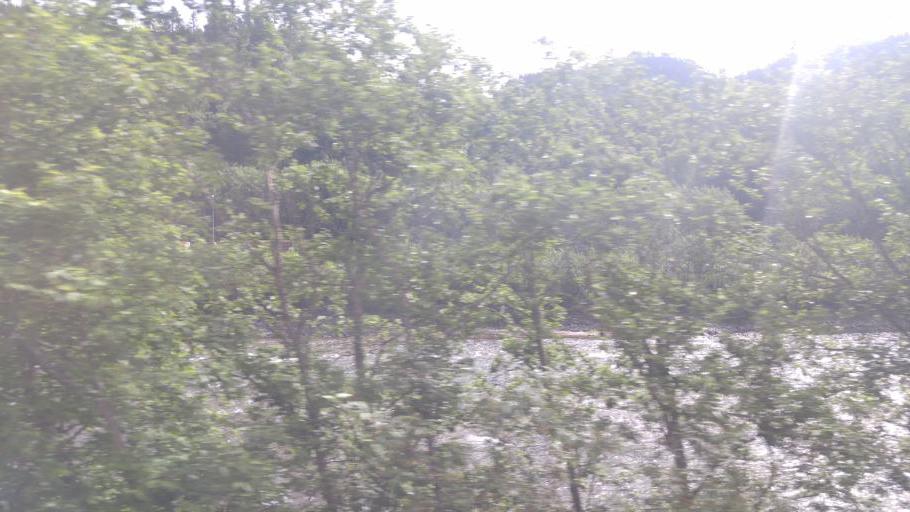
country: NO
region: Sor-Trondelag
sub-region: Midtre Gauldal
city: Storen
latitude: 63.0622
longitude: 10.2881
